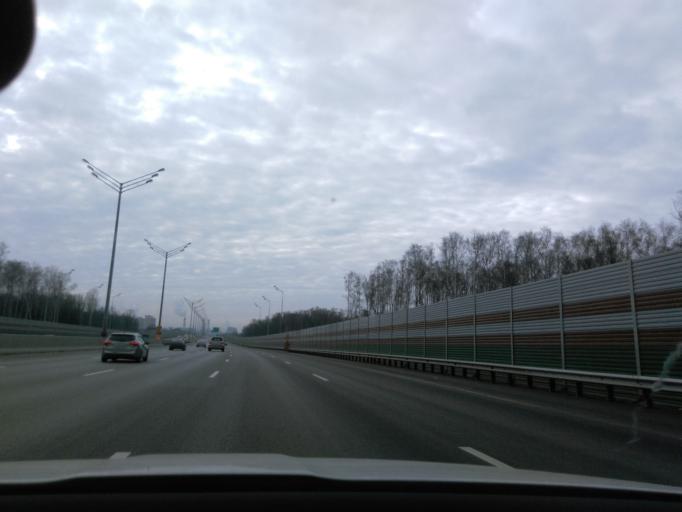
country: RU
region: Moscow
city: Khimki
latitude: 55.9161
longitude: 37.4599
